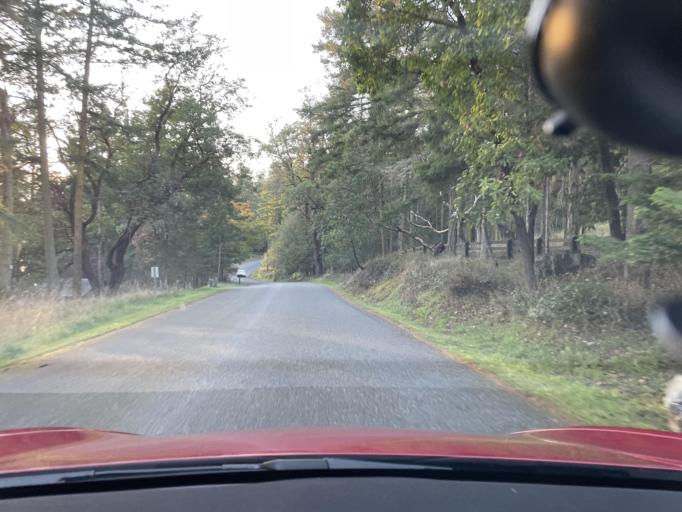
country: US
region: Washington
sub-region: San Juan County
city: Friday Harbor
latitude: 48.6127
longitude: -123.1510
